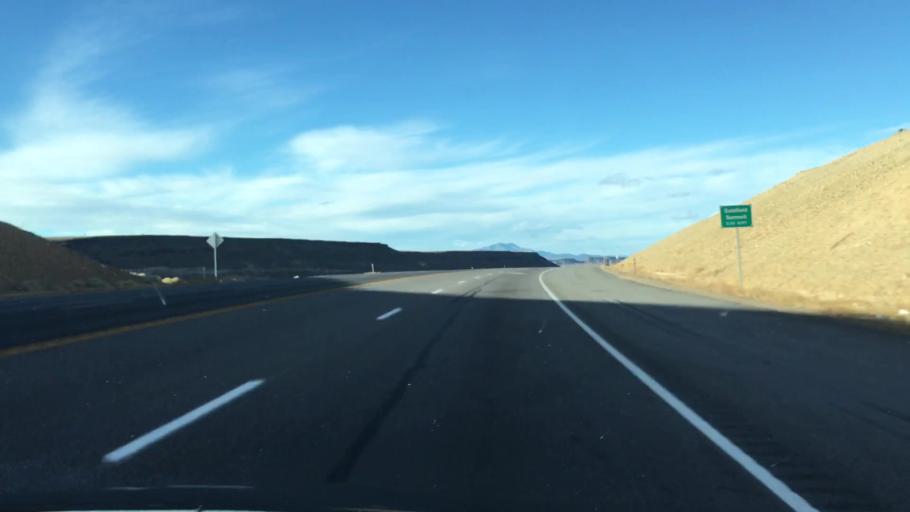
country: US
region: Nevada
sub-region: Esmeralda County
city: Goldfield
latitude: 37.6797
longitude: -117.2280
